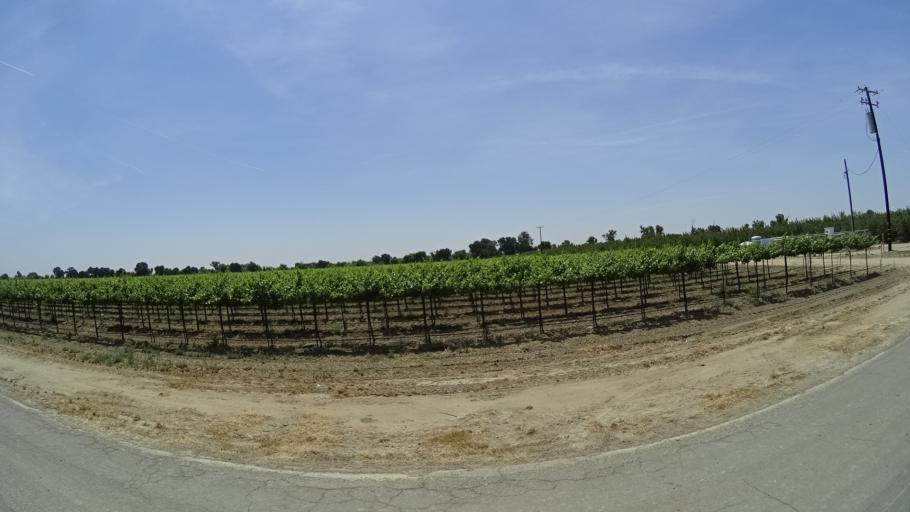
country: US
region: California
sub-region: Fresno County
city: Riverdale
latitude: 36.3875
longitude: -119.8643
